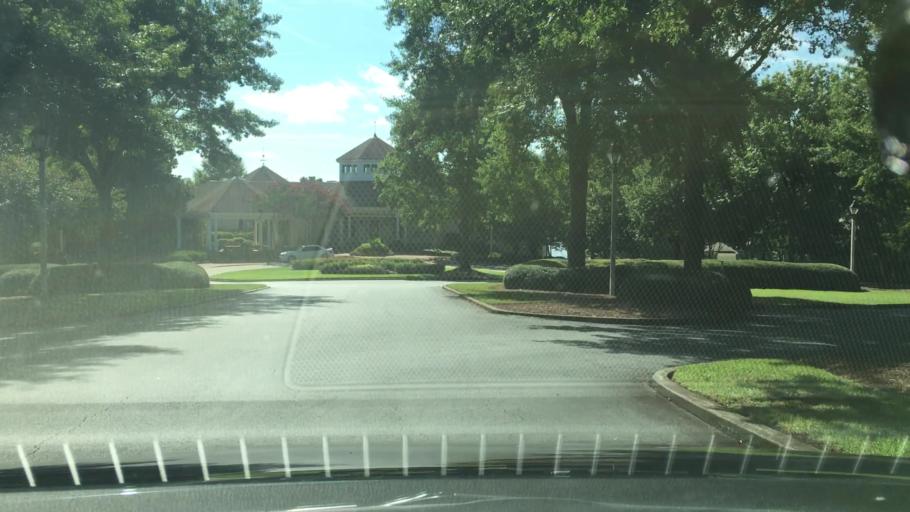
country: US
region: Georgia
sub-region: Putnam County
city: Jefferson
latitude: 33.3938
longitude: -83.2331
